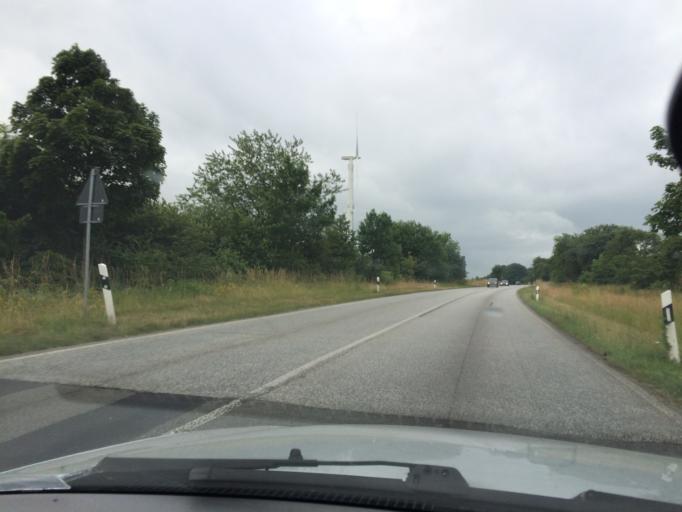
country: DE
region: Schleswig-Holstein
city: Oeversee
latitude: 54.6641
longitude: 9.4428
